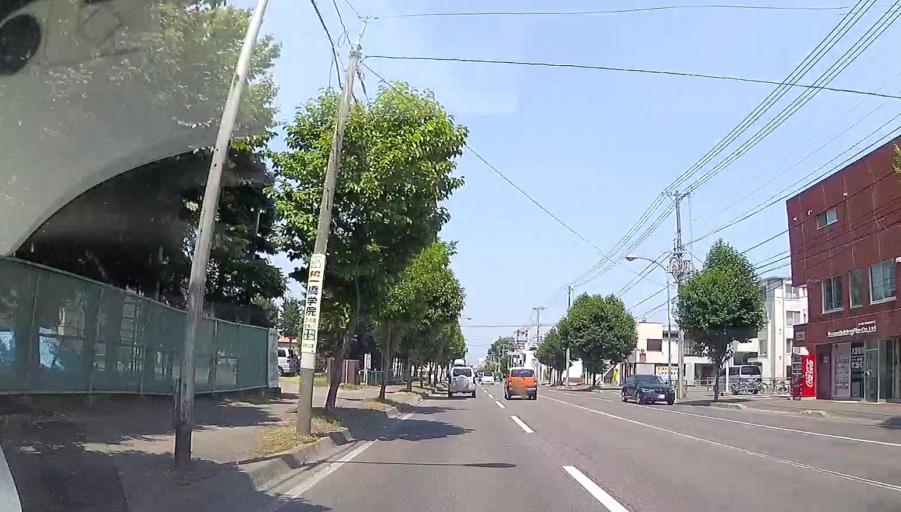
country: JP
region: Hokkaido
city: Obihiro
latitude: 42.9025
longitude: 143.1999
